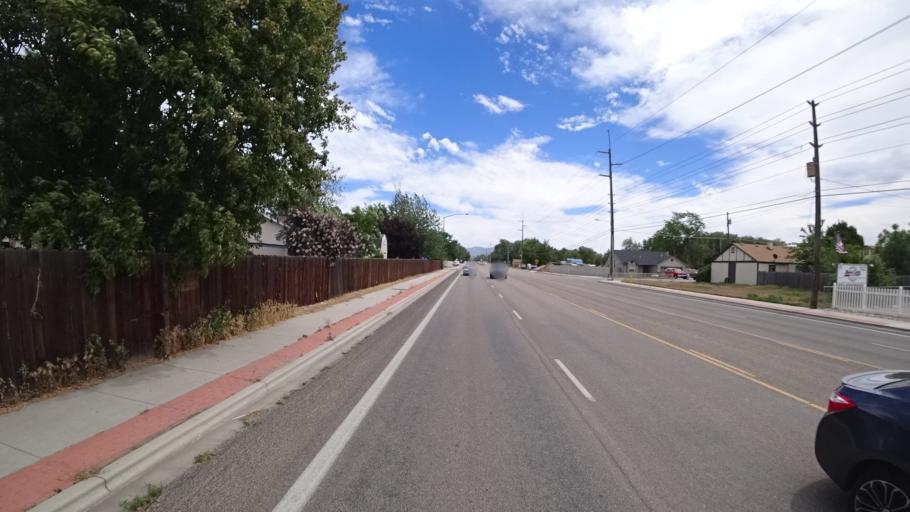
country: US
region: Idaho
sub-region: Ada County
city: Garden City
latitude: 43.6341
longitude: -116.3021
